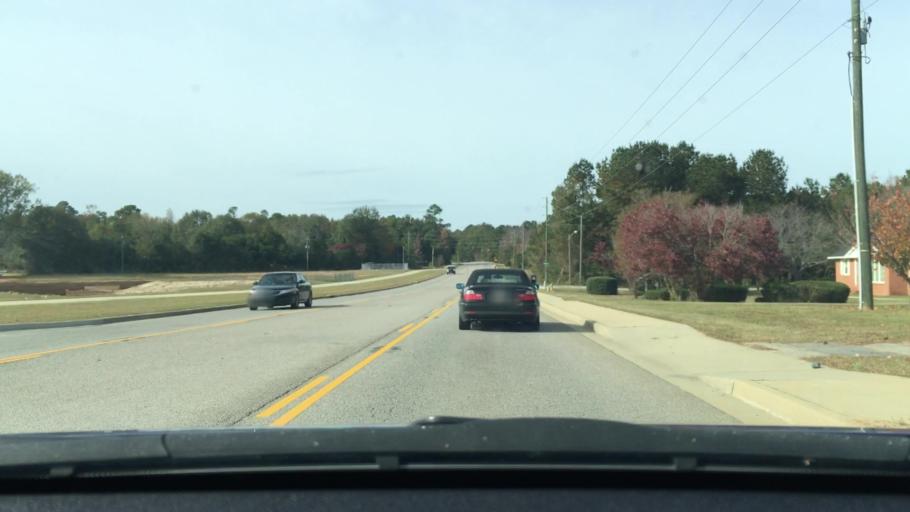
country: US
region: South Carolina
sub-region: Sumter County
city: South Sumter
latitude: 33.9224
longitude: -80.3988
